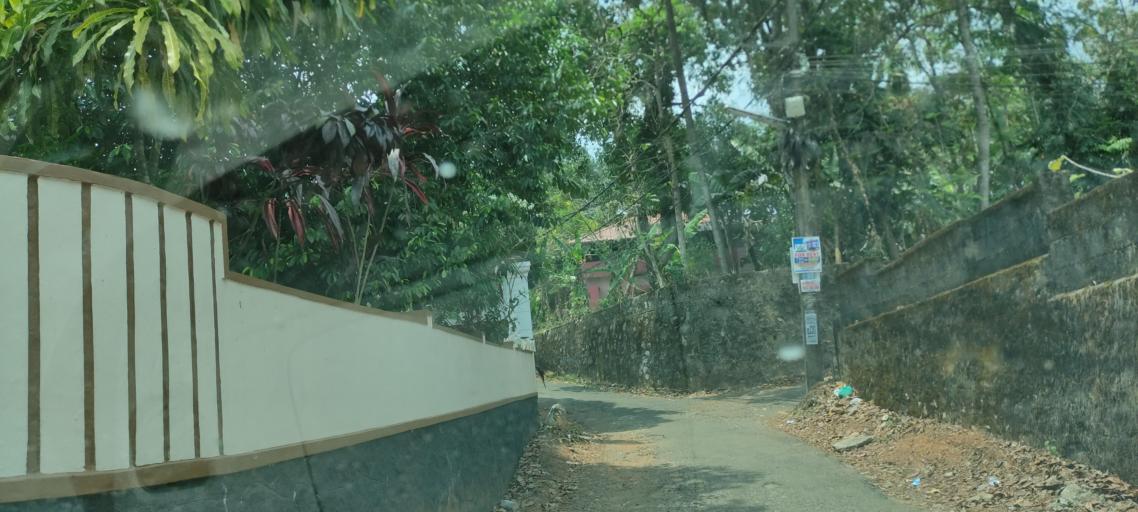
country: IN
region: Kerala
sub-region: Pattanamtitta
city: Adur
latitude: 9.1512
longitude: 76.7309
